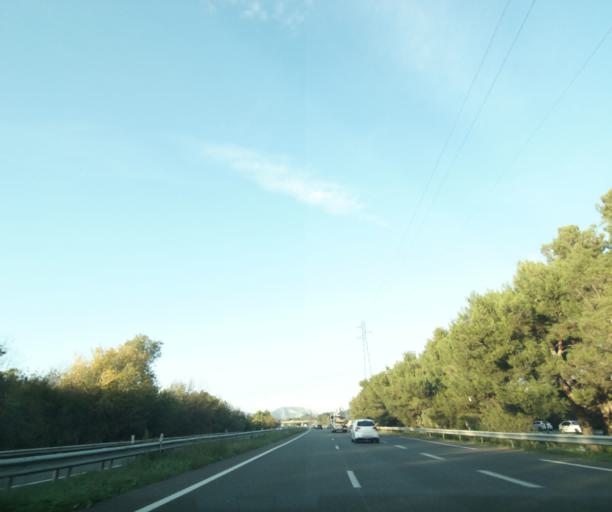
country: FR
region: Provence-Alpes-Cote d'Azur
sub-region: Departement des Bouches-du-Rhone
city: Aubagne
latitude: 43.3022
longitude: 5.5911
